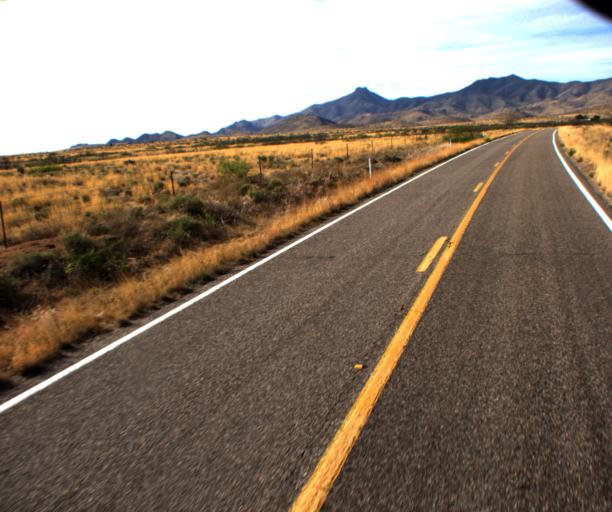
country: US
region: Arizona
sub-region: Cochise County
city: Willcox
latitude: 32.1223
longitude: -109.5556
